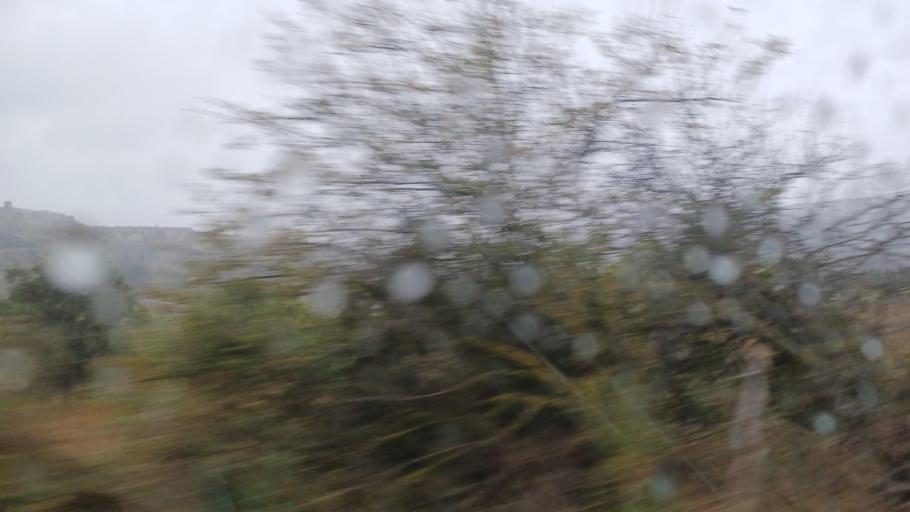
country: CY
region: Pafos
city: Tala
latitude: 34.8925
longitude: 32.4645
